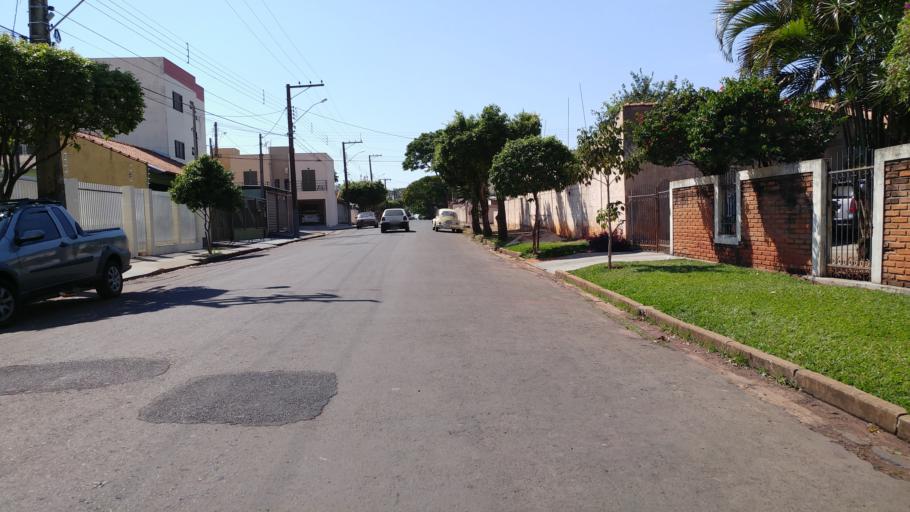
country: BR
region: Sao Paulo
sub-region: Paraguacu Paulista
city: Paraguacu Paulista
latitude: -22.4144
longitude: -50.5853
